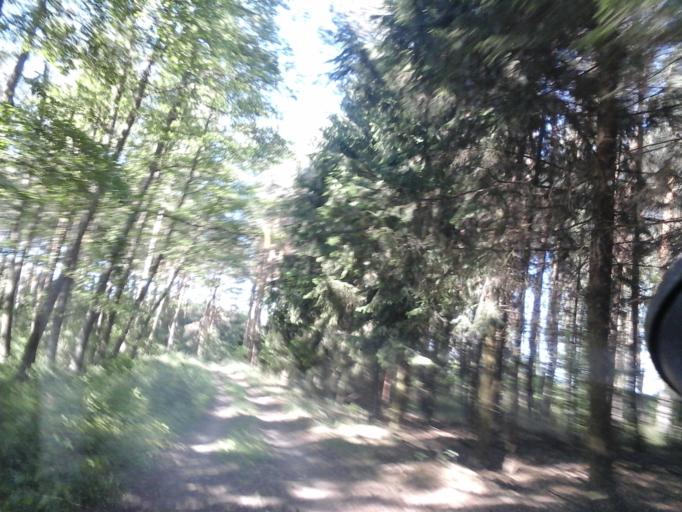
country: PL
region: West Pomeranian Voivodeship
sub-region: Powiat choszczenski
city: Recz
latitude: 53.1927
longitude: 15.5257
